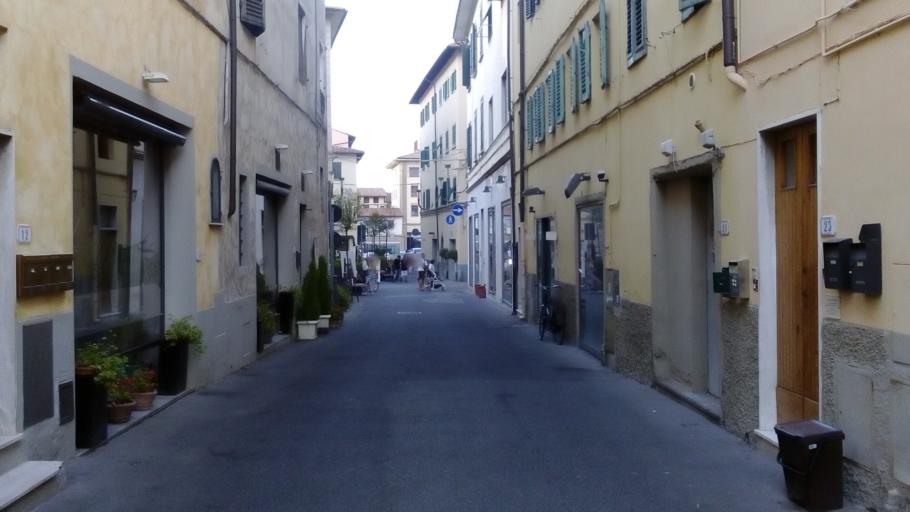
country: IT
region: Tuscany
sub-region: Province of Florence
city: Empoli
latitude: 43.7189
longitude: 10.9484
